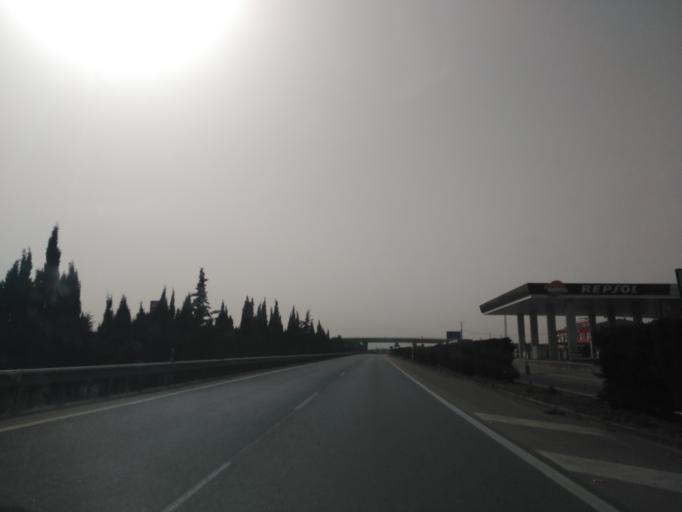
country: ES
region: Castille and Leon
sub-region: Provincia de Valladolid
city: Cubillas de Santa Marta
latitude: 41.8103
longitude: -4.5831
